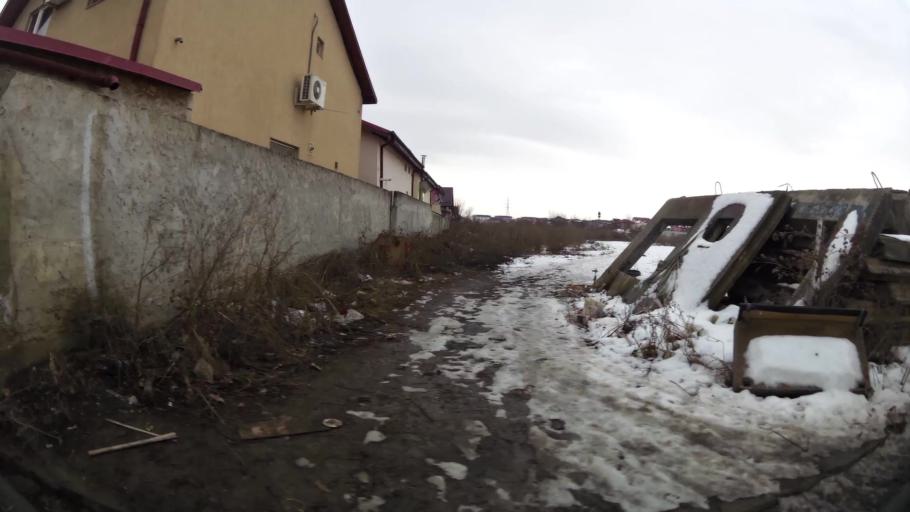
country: RO
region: Ilfov
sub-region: Comuna Pantelimon
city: Pantelimon
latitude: 44.4592
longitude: 26.2165
